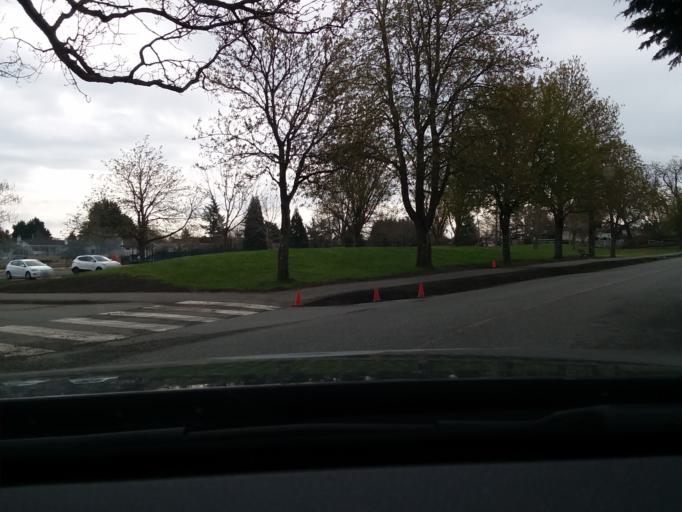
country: CA
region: British Columbia
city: Oak Bay
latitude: 48.4774
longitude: -123.3284
